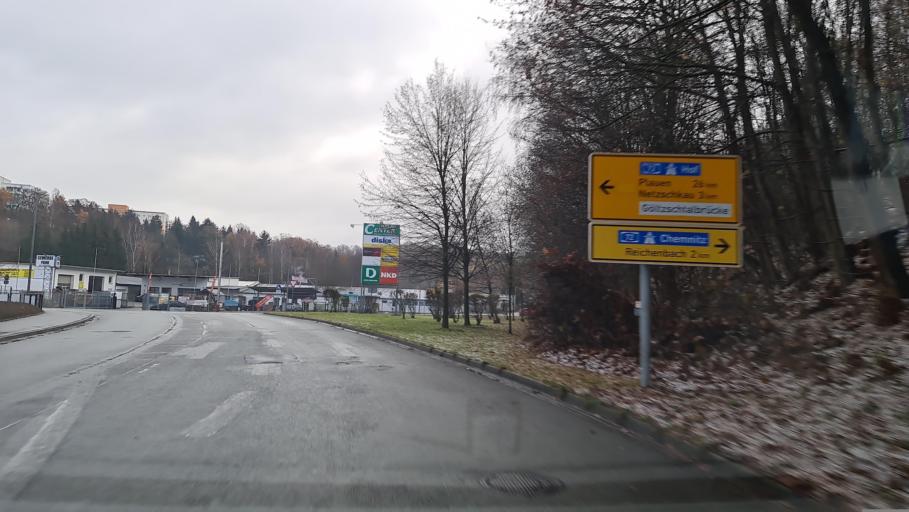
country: DE
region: Saxony
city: Mylau
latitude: 50.6186
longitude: 12.2739
